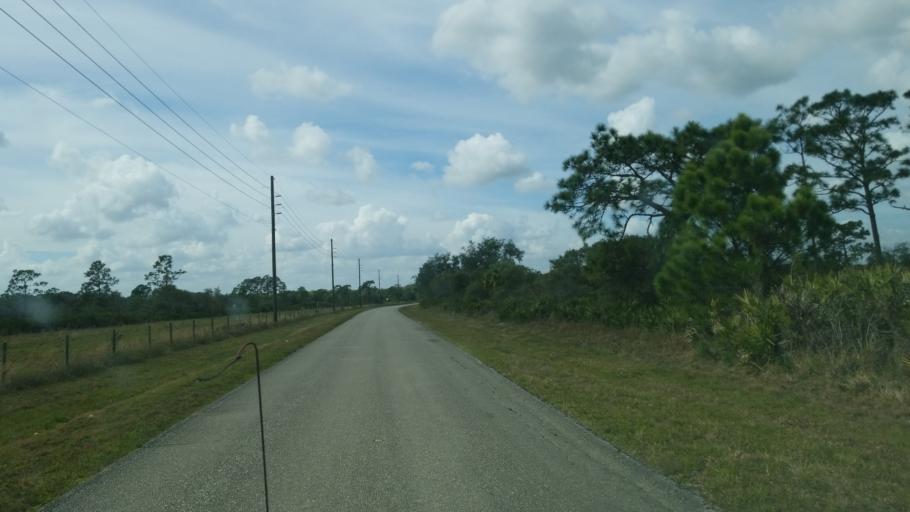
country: US
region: Florida
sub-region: Okeechobee County
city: Cypress Quarters
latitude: 27.5187
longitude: -80.7879
